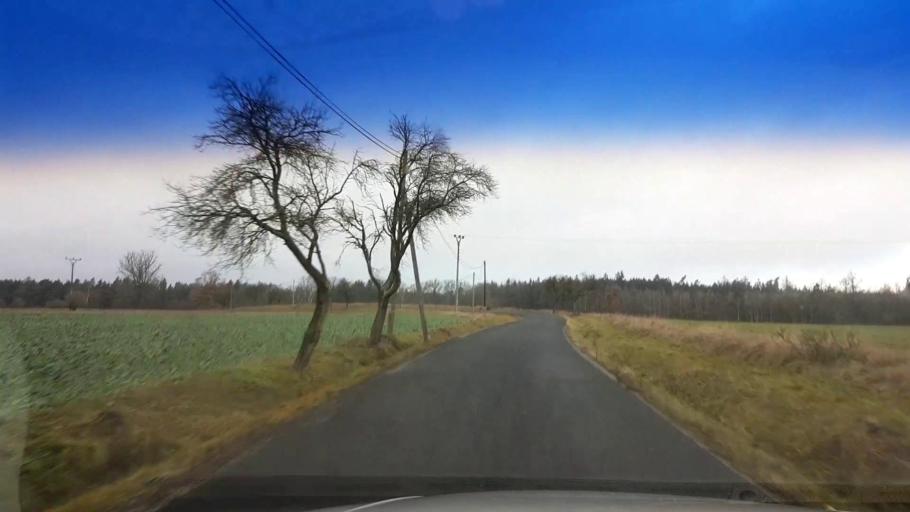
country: CZ
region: Karlovarsky
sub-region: Okres Cheb
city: Cheb
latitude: 50.0400
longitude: 12.3657
